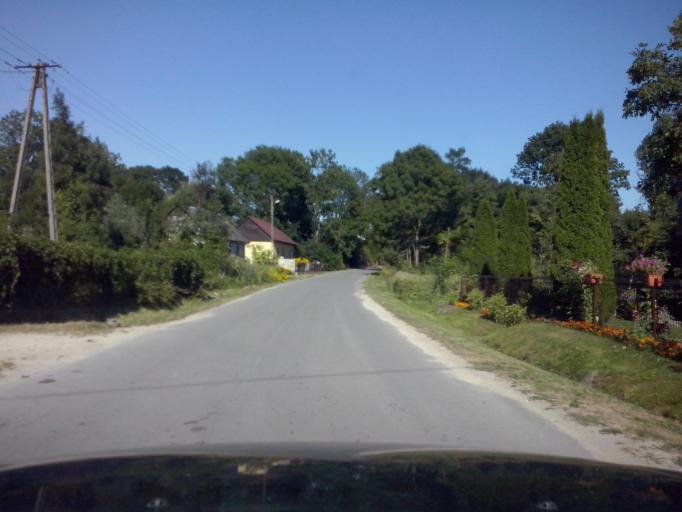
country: PL
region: Swietokrzyskie
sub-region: Powiat pinczowski
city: Kije
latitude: 50.5804
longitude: 20.6514
